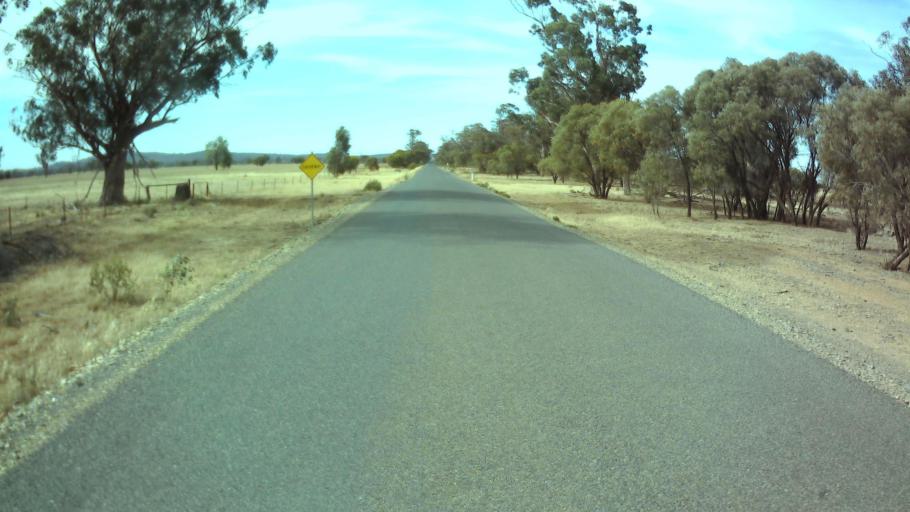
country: AU
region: New South Wales
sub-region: Weddin
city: Grenfell
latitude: -33.8746
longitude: 147.8573
